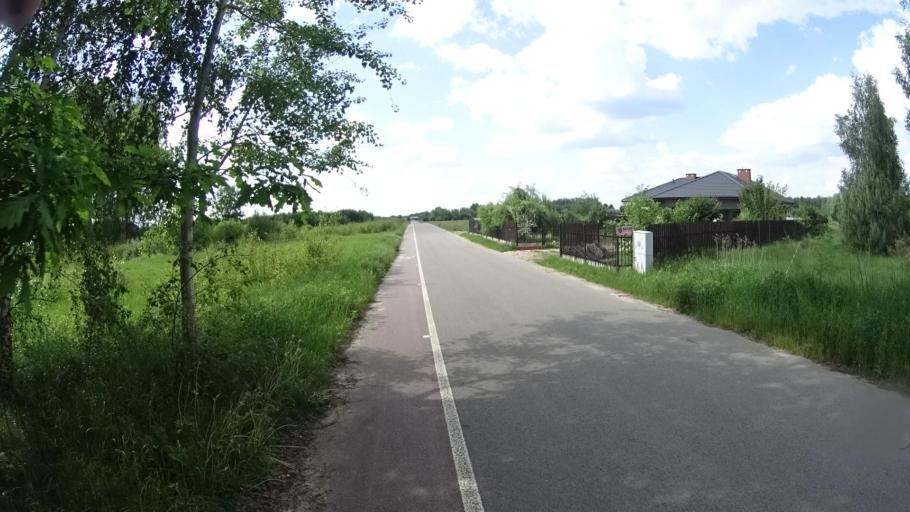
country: PL
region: Masovian Voivodeship
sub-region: Powiat piaseczynski
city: Tarczyn
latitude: 52.0017
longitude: 20.8328
